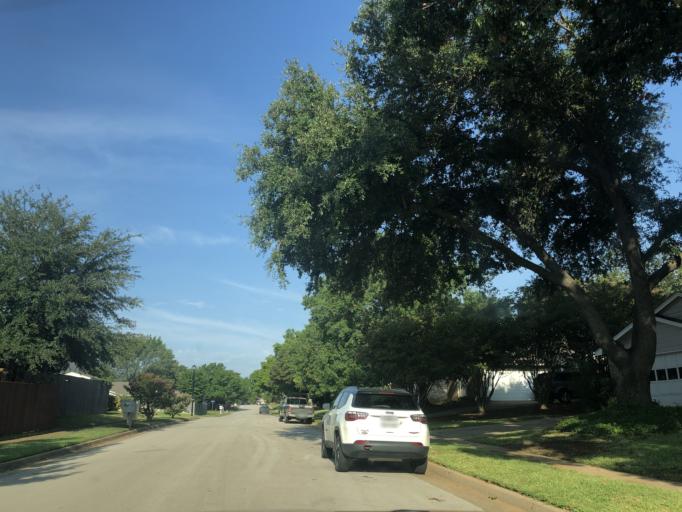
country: US
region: Texas
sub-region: Tarrant County
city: Euless
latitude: 32.8752
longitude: -97.0867
